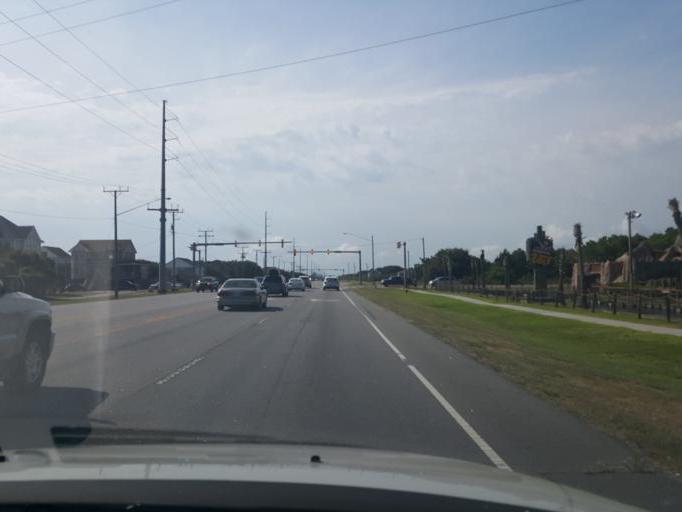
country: US
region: North Carolina
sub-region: Dare County
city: Kill Devil Hills
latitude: 36.0293
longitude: -75.6703
